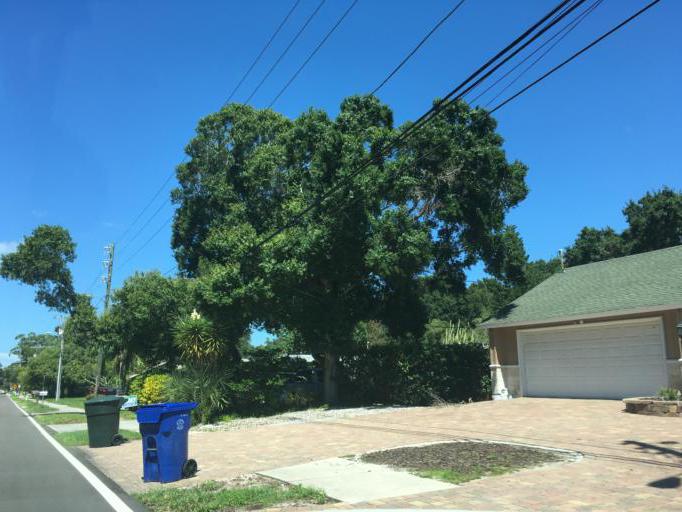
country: US
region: Florida
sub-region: Pinellas County
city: Dunedin
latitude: 28.0378
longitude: -82.7748
